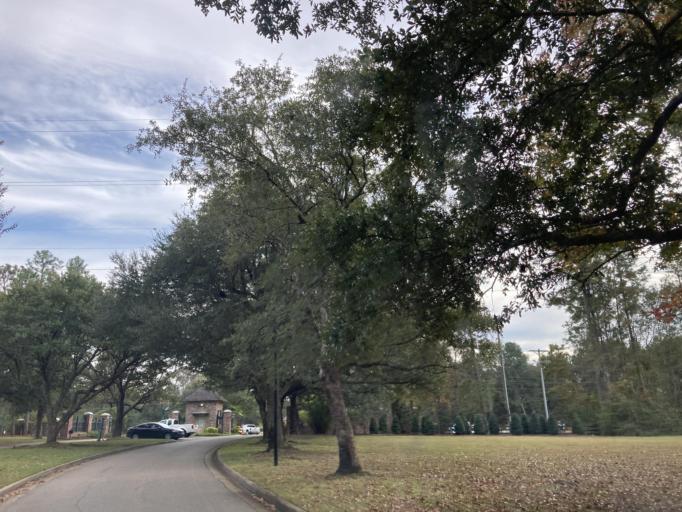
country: US
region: Mississippi
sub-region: Lamar County
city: West Hattiesburg
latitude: 31.3152
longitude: -89.4569
